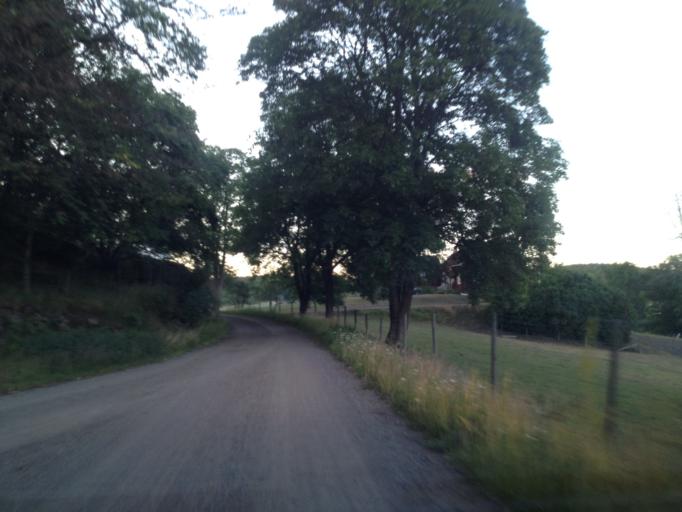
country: SE
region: Kalmar
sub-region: Vasterviks Kommun
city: Overum
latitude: 57.9915
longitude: 16.1782
